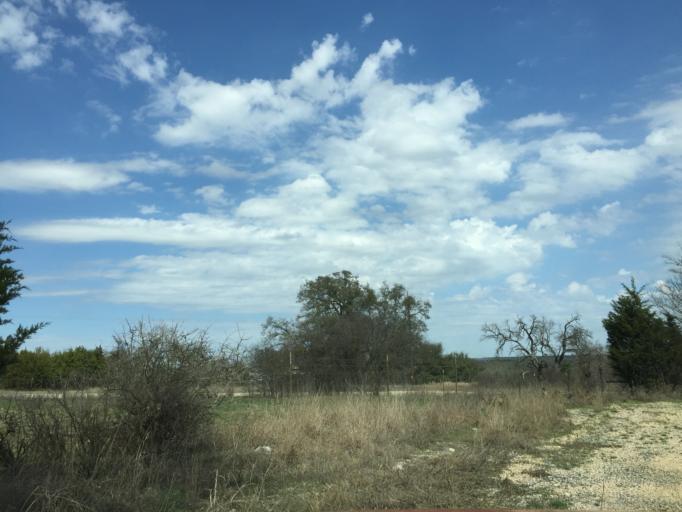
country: US
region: Texas
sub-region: Burnet County
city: Bertram
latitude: 30.7512
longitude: -97.9388
